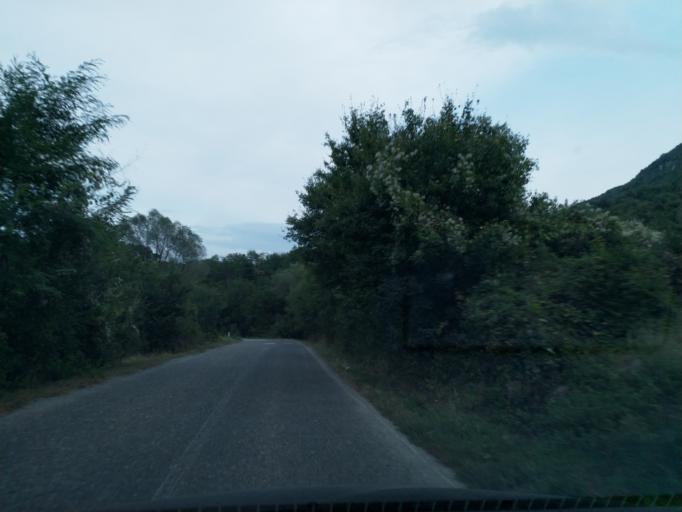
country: RS
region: Central Serbia
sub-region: Pomoravski Okrug
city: Paracin
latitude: 43.8565
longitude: 21.5318
